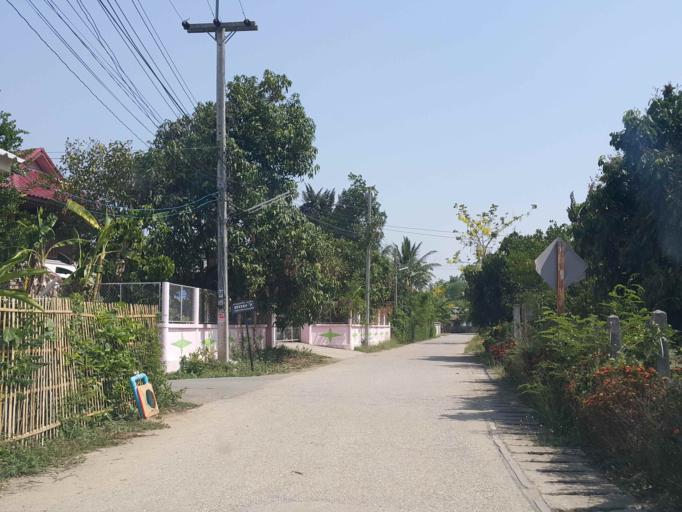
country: TH
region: Chiang Mai
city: San Kamphaeng
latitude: 18.7857
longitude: 99.1123
